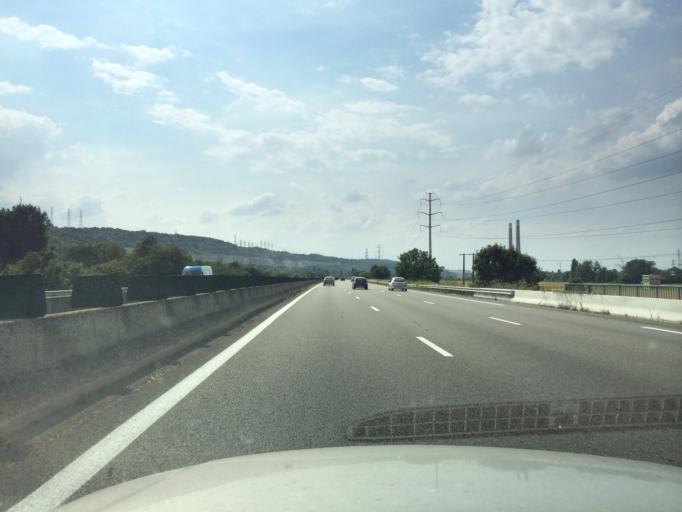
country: FR
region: Ile-de-France
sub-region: Departement des Yvelines
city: Mezieres-sur-Seine
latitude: 48.9639
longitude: 1.7898
